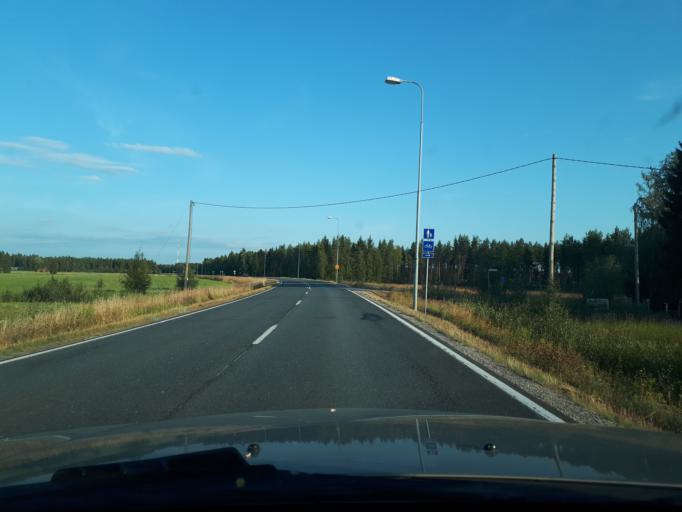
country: FI
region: Northern Ostrobothnia
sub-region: Oulu
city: Oulunsalo
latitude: 64.9809
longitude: 25.2725
